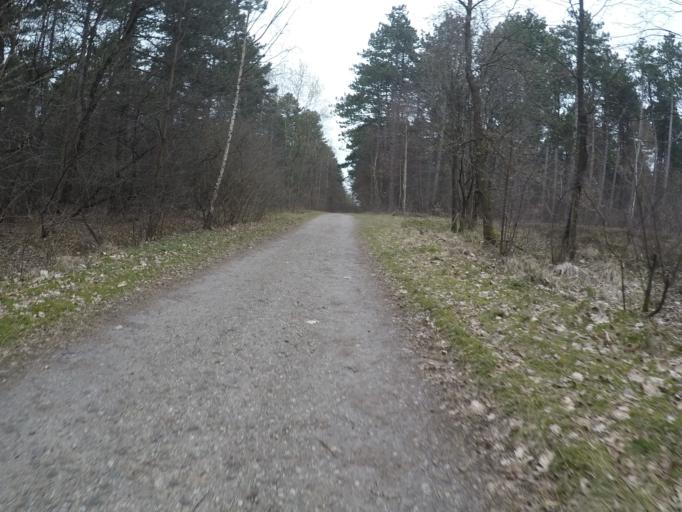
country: DE
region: Lower Saxony
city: Nordholz
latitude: 53.8208
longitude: 8.6443
